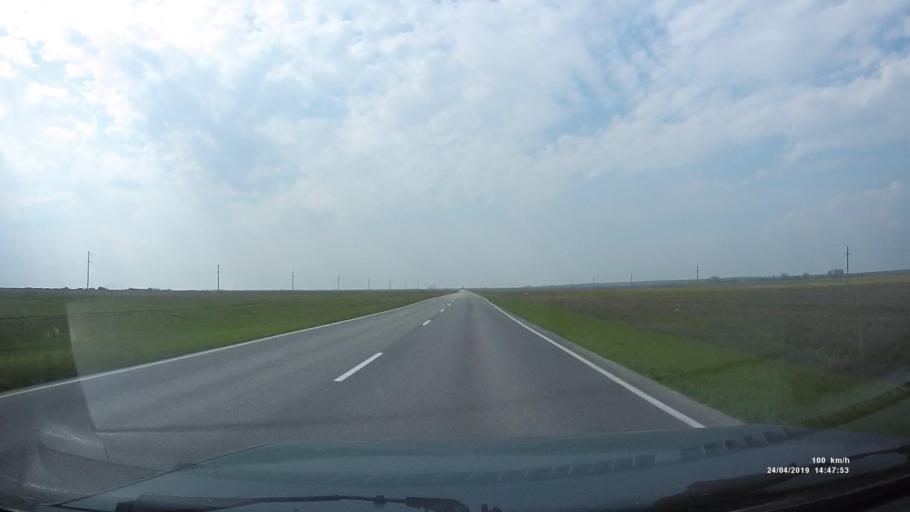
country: RU
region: Rostov
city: Remontnoye
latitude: 46.4957
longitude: 43.7654
